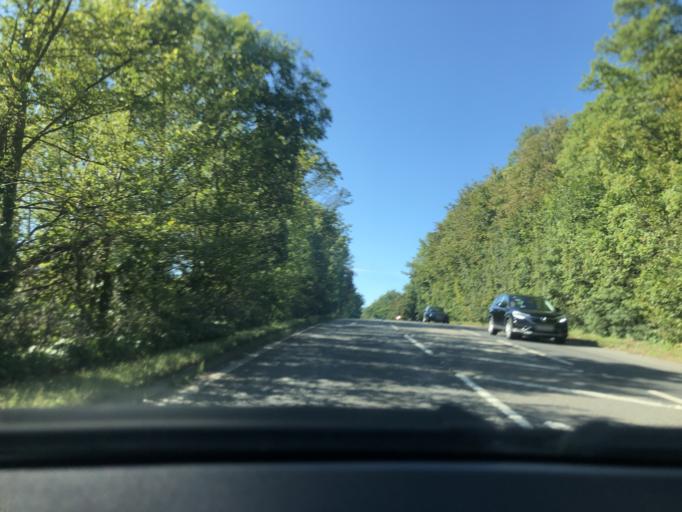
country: GB
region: England
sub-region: Somerset
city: Puriton
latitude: 51.1632
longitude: -2.9693
